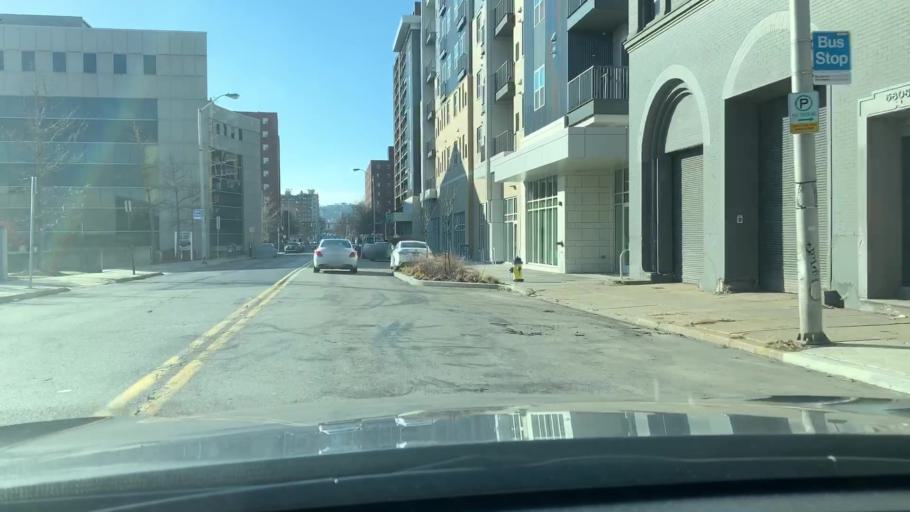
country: US
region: Pennsylvania
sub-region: Allegheny County
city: Bloomfield
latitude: 40.4556
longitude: -79.9350
